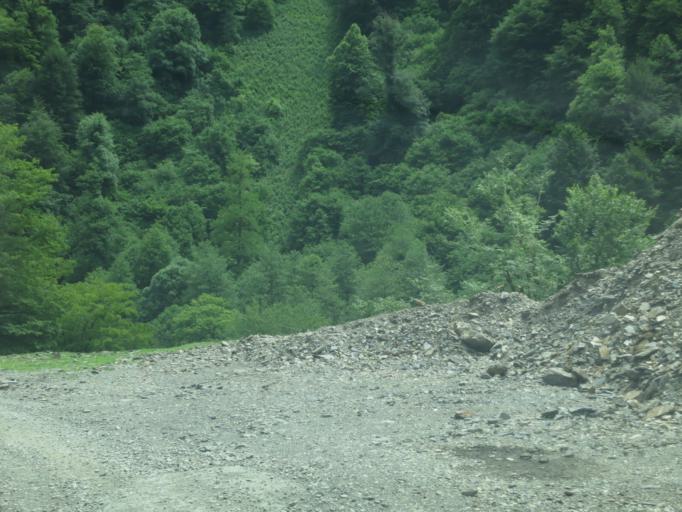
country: GE
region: Kakheti
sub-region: Telavi
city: Telavi
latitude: 42.1950
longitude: 45.4609
